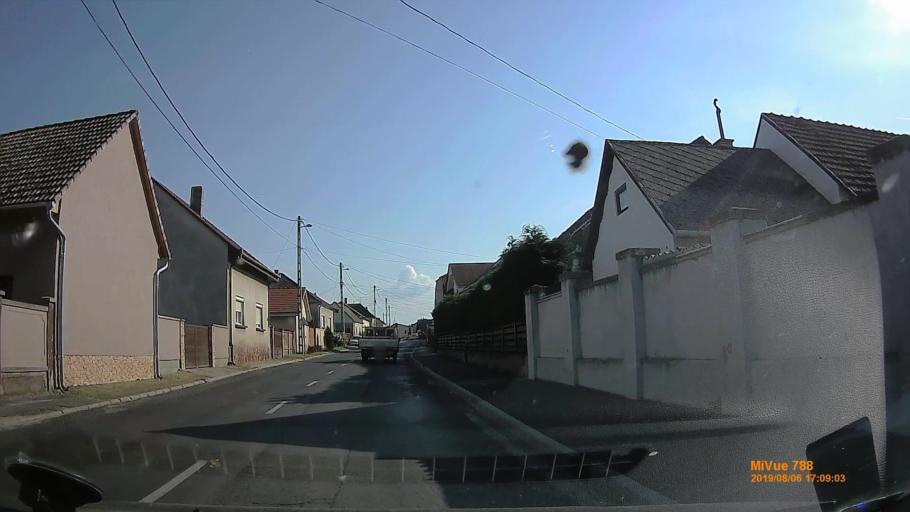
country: HU
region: Zala
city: Nagykanizsa
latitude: 46.4552
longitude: 16.9572
